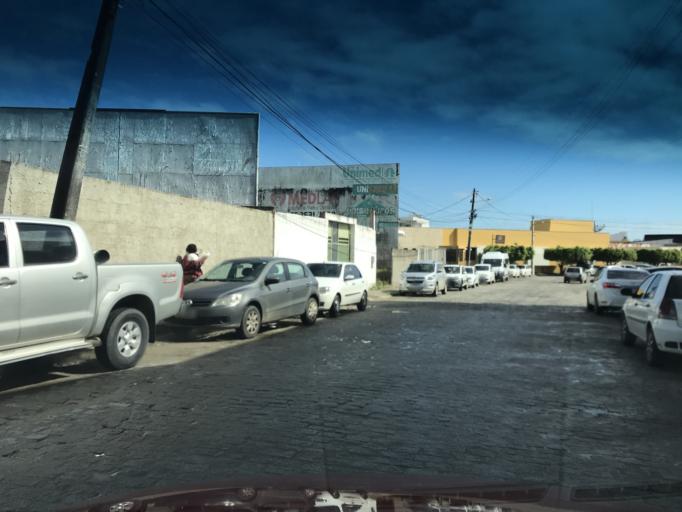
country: BR
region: Bahia
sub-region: Santo Antonio De Jesus
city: Santo Antonio de Jesus
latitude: -12.9647
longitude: -39.2643
